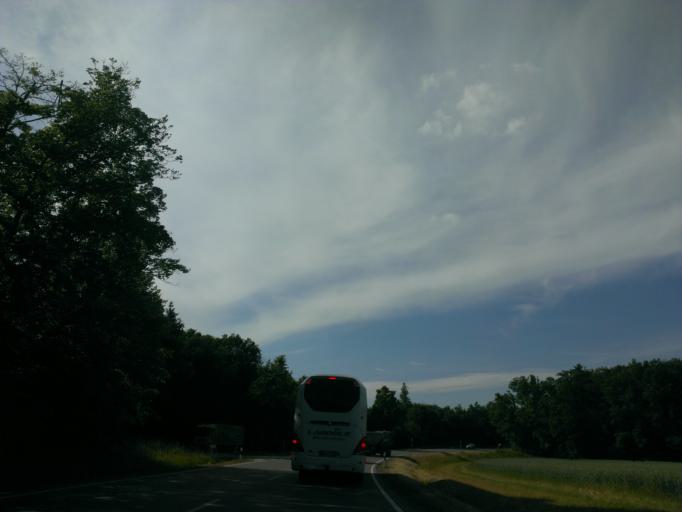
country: DE
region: Bavaria
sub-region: Swabia
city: Fremdingen
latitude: 48.9578
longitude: 10.4491
